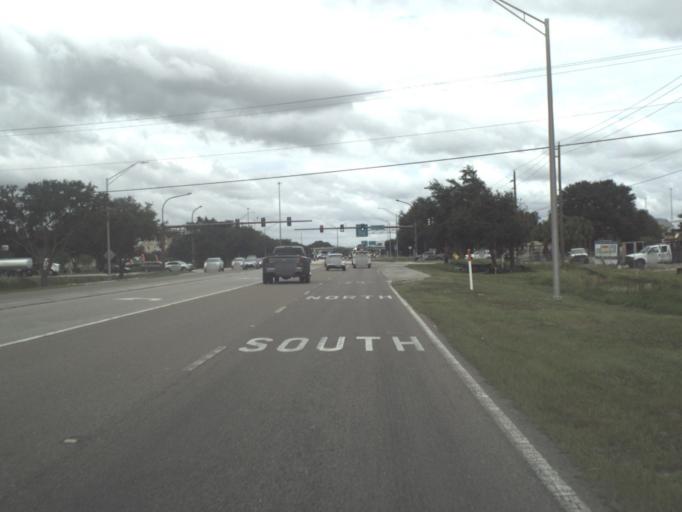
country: US
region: Florida
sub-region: Sarasota County
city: Plantation
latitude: 27.1046
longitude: -82.3843
